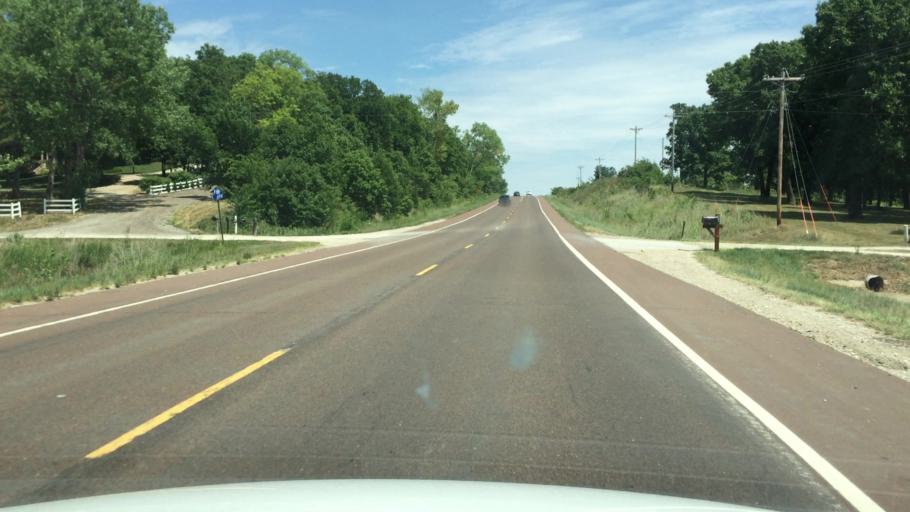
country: US
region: Kansas
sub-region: Douglas County
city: Lawrence
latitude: 38.9713
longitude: -95.3915
